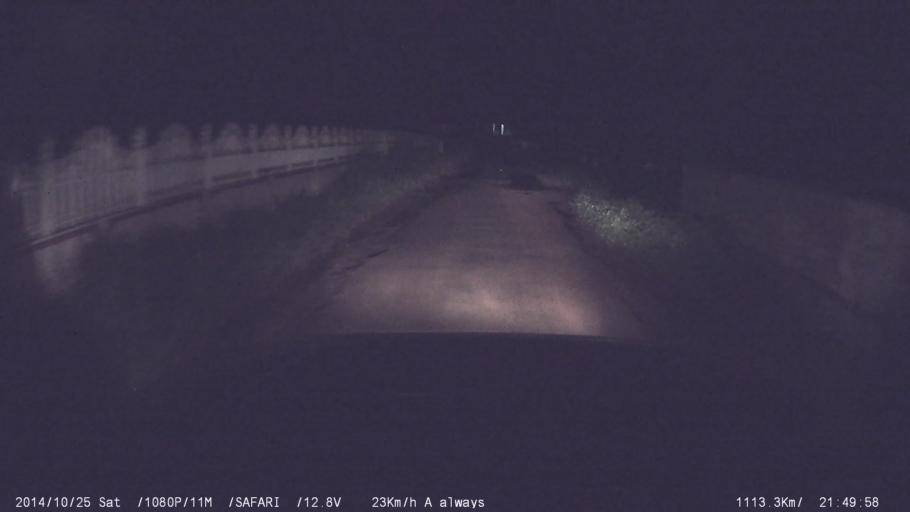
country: IN
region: Kerala
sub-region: Kottayam
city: Kottayam
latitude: 9.6333
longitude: 76.5449
